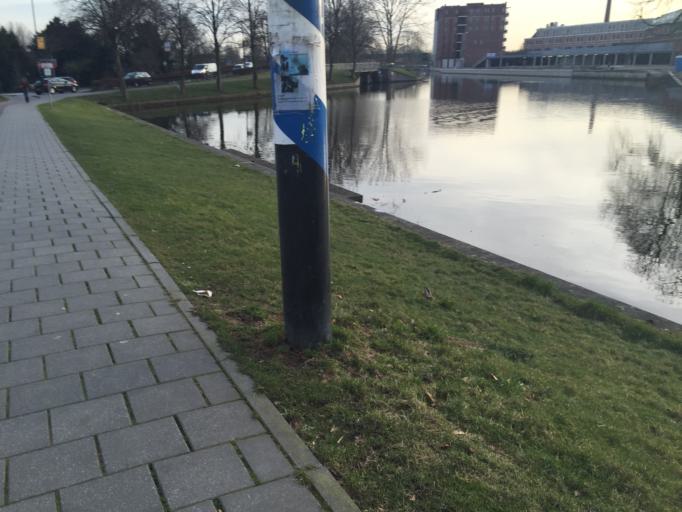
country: NL
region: Utrecht
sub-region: Gemeente Woerden
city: Woerden
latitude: 52.0867
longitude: 4.8912
